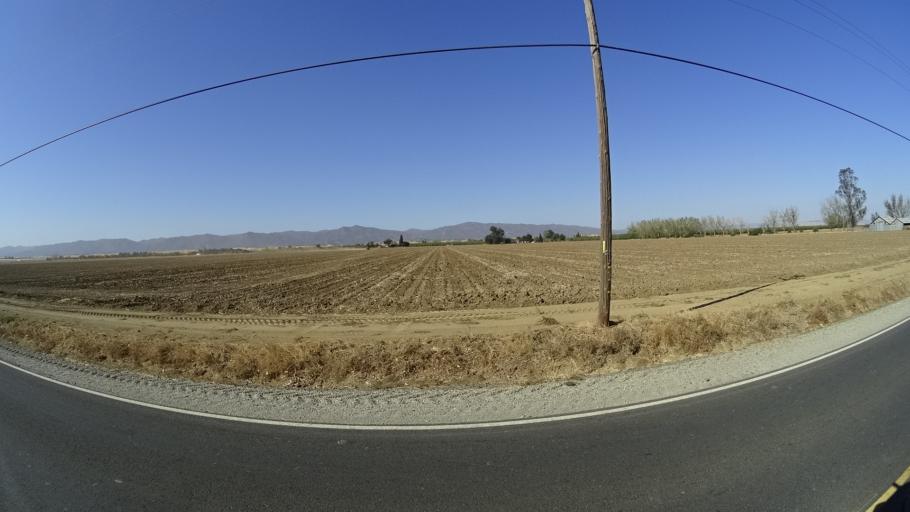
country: US
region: California
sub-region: Yolo County
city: Cottonwood
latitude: 38.6333
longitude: -121.9711
